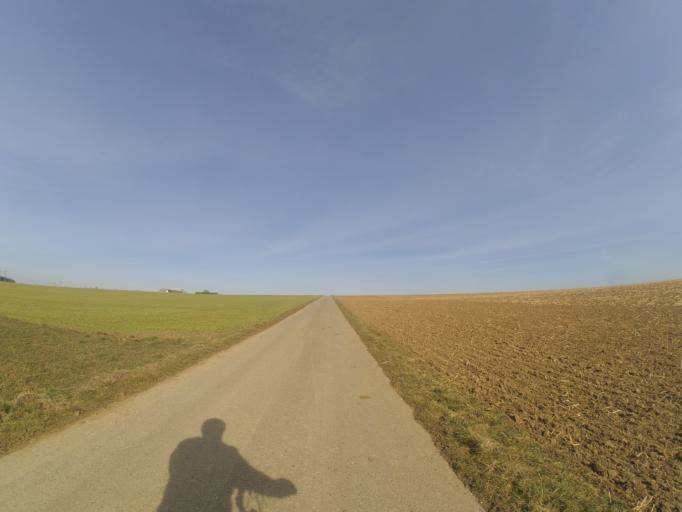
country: DE
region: Baden-Wuerttemberg
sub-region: Tuebingen Region
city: Beimerstetten
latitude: 48.4650
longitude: 9.9970
